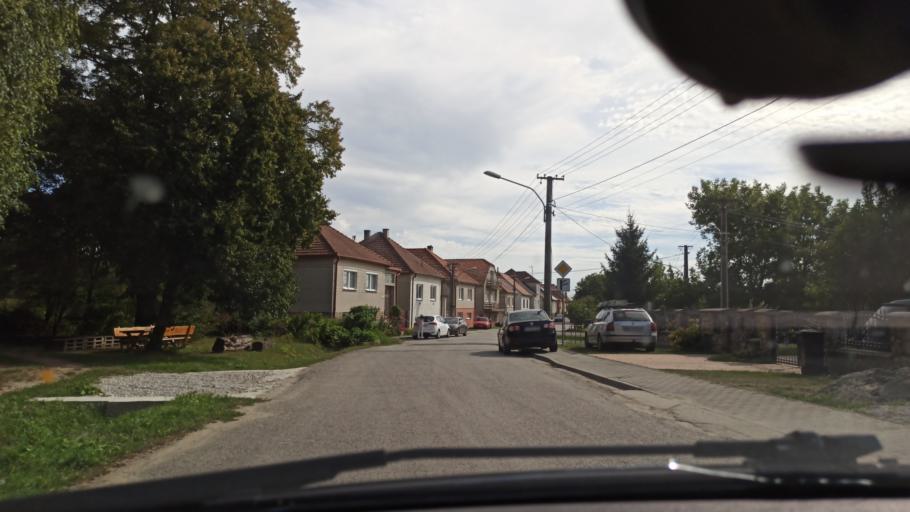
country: SK
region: Trnavsky
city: Gbely
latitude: 48.6841
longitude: 17.2038
